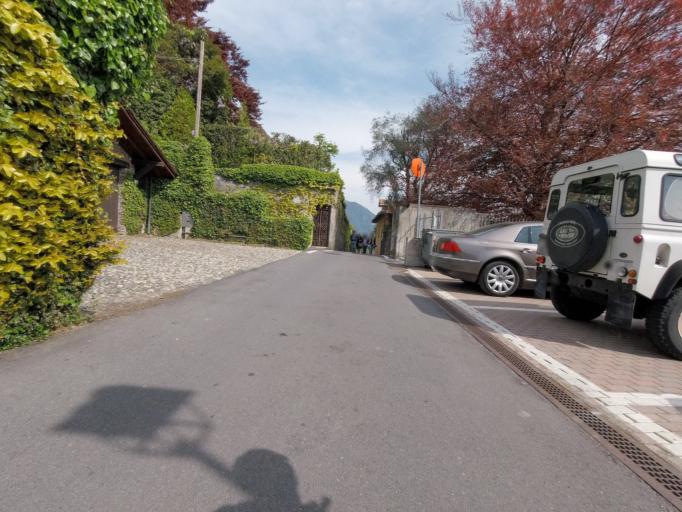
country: IT
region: Lombardy
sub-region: Provincia di Como
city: Griante
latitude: 45.9930
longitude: 9.2335
